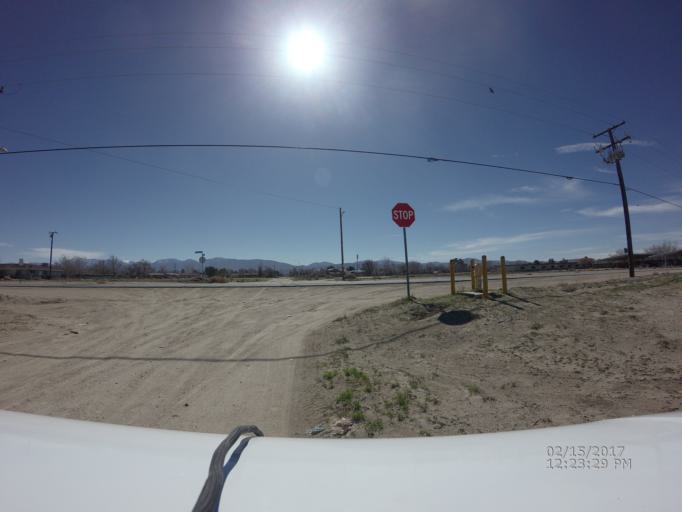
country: US
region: California
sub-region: Los Angeles County
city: Littlerock
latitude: 34.5800
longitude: -117.9563
